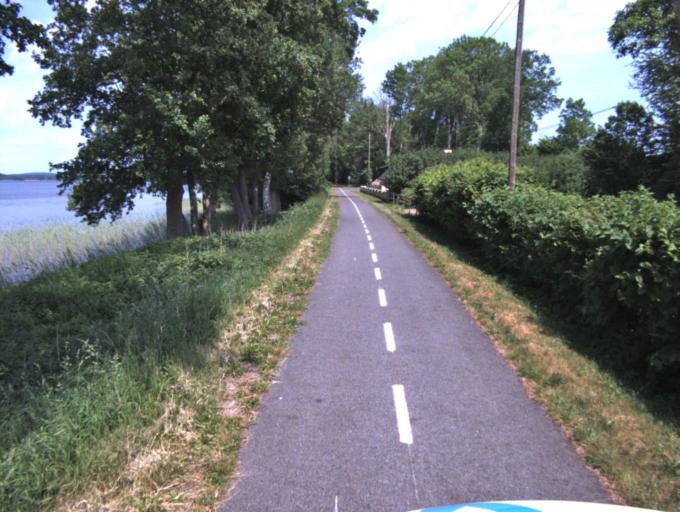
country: SE
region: Skane
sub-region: Kristianstads Kommun
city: Fjalkinge
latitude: 56.0818
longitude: 14.2243
